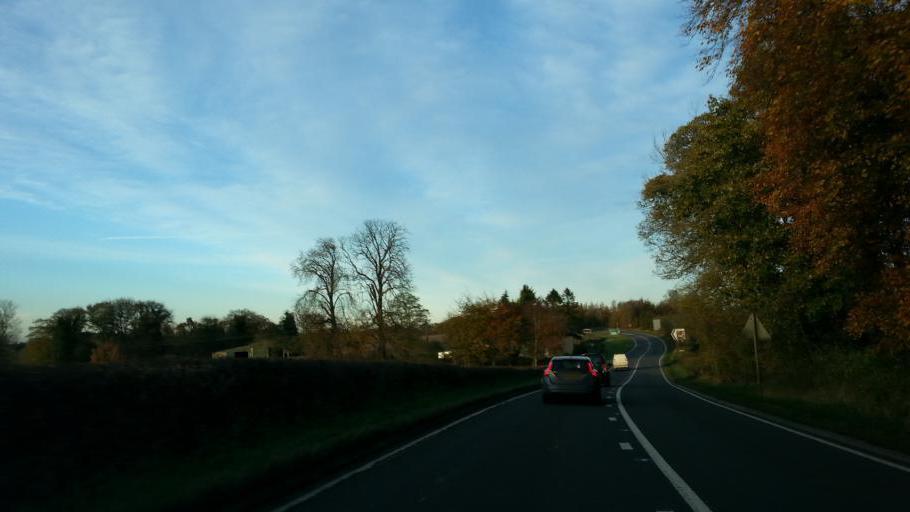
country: GB
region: England
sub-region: District of Rutland
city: Morcott
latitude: 52.5232
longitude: -0.5915
